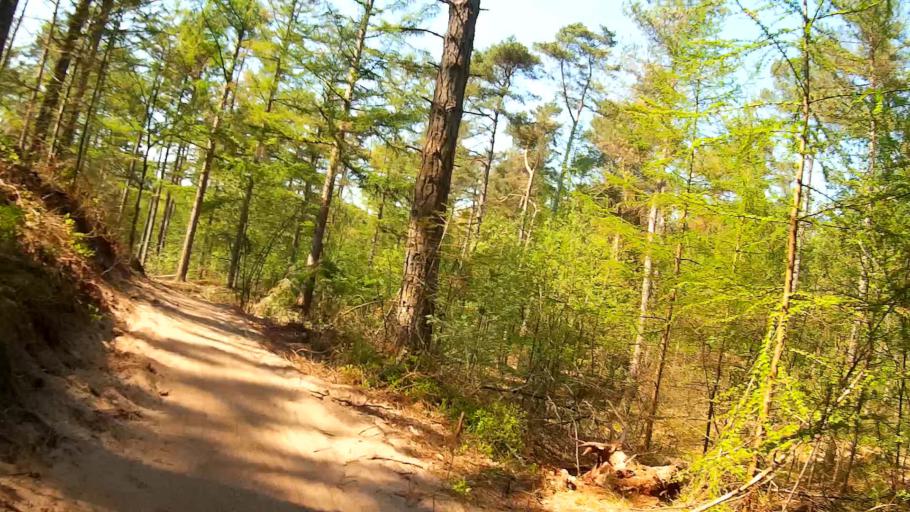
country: NL
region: Utrecht
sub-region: Gemeente Baarn
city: Baarn
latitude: 52.2010
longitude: 5.2686
